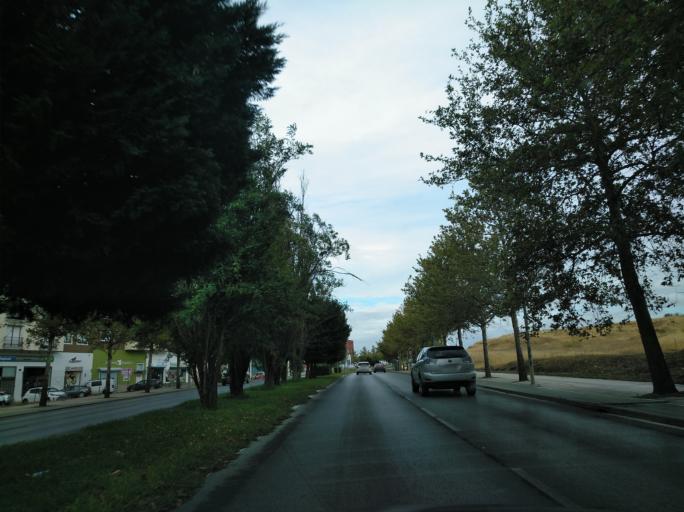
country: ES
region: Extremadura
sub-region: Provincia de Badajoz
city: Badajoz
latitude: 38.8645
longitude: -6.9785
